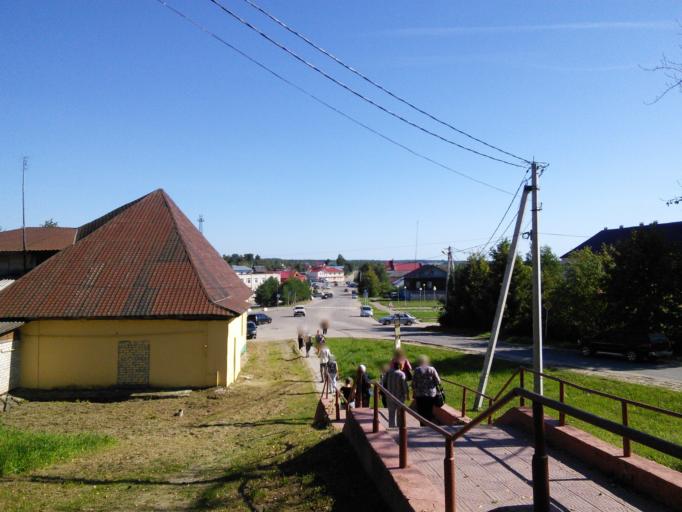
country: RU
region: Tverskaya
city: Kesova Gora
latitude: 57.5805
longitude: 37.2900
